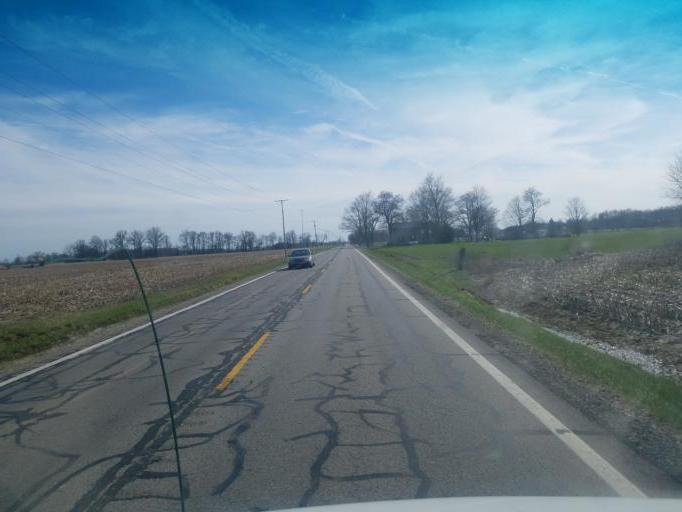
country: US
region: Ohio
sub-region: Marion County
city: Prospect
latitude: 40.4564
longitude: -83.2165
